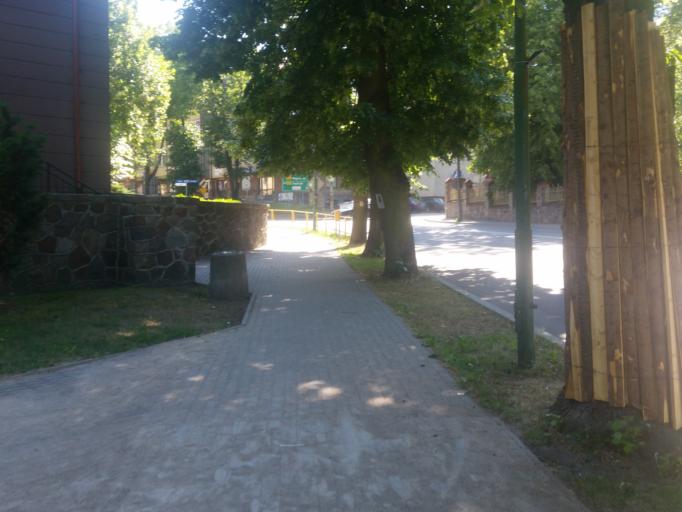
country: PL
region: Warmian-Masurian Voivodeship
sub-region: Powiat goldapski
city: Goldap
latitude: 54.3094
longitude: 22.3043
